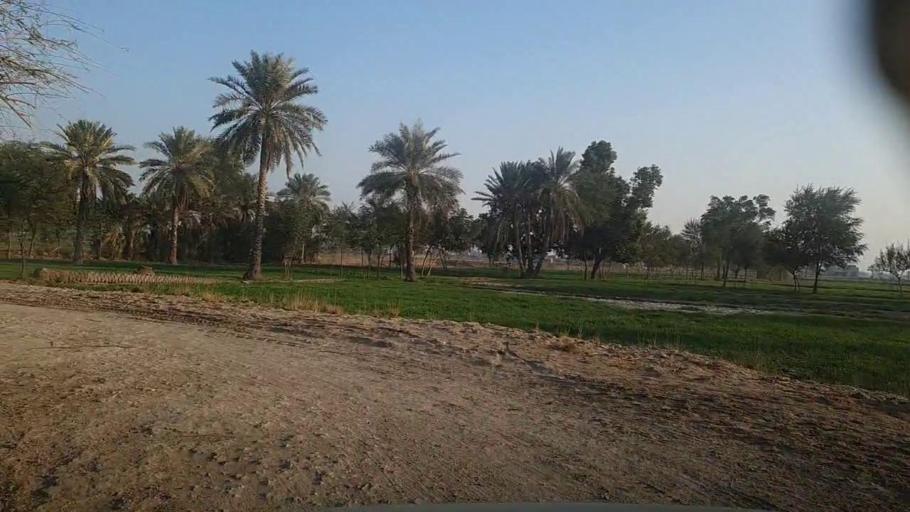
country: PK
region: Sindh
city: Khairpur
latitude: 28.0677
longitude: 69.7511
